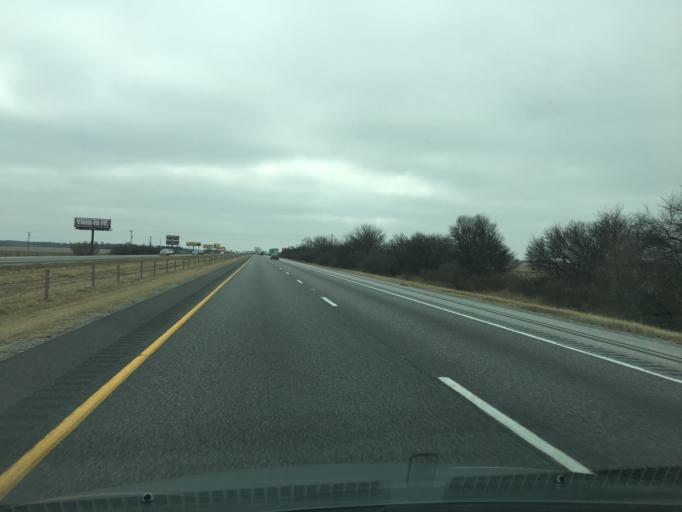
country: US
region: Indiana
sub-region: Jasper County
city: Remington
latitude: 40.8250
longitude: -87.1668
